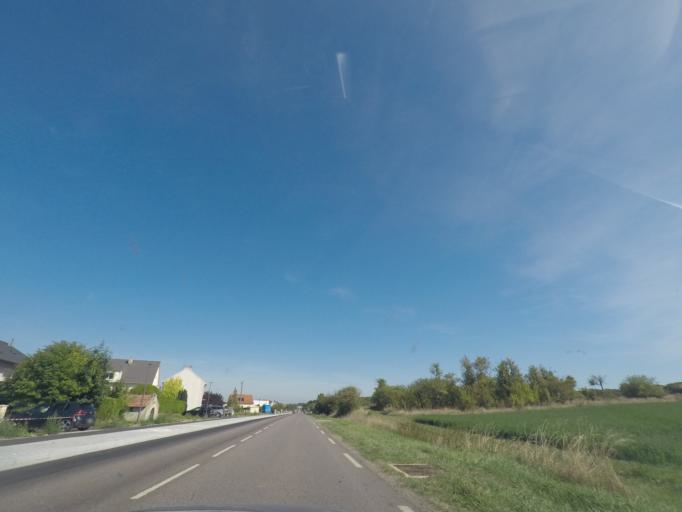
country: FR
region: Lorraine
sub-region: Departement de la Moselle
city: Hettange-Grande
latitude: 49.4144
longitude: 6.1569
